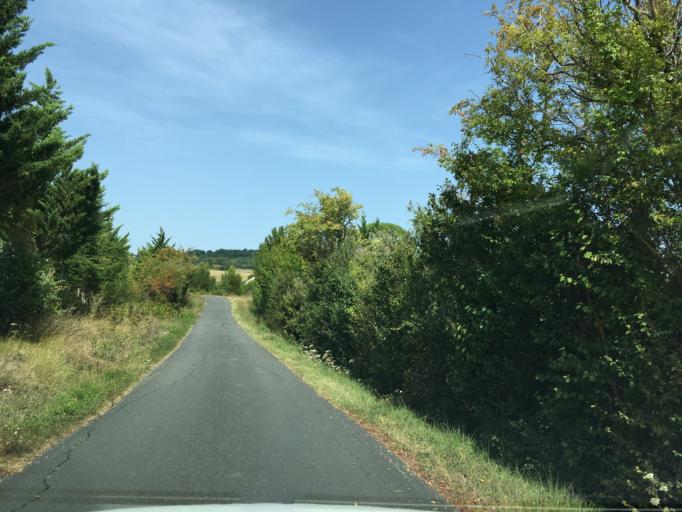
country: FR
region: Midi-Pyrenees
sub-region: Departement du Tarn
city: Castres
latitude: 43.6409
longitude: 2.2363
